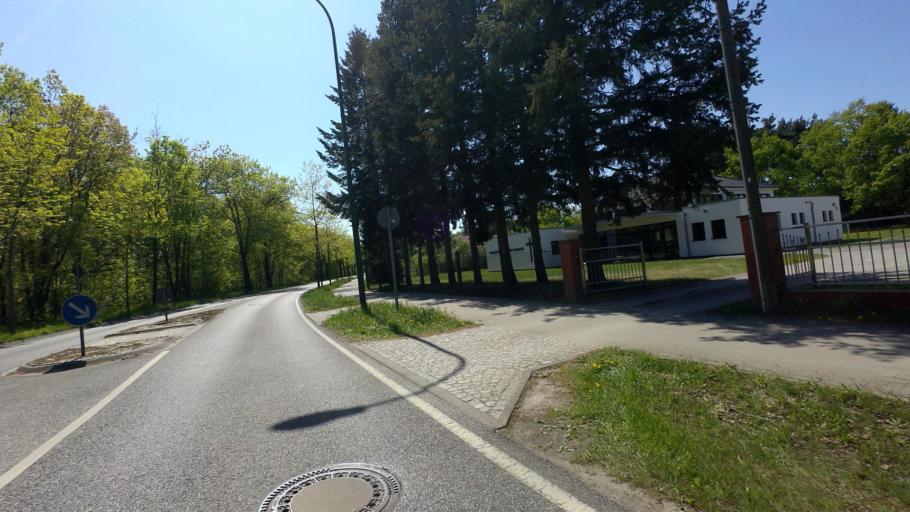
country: DE
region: Brandenburg
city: Bestensee
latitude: 52.2675
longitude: 13.6342
